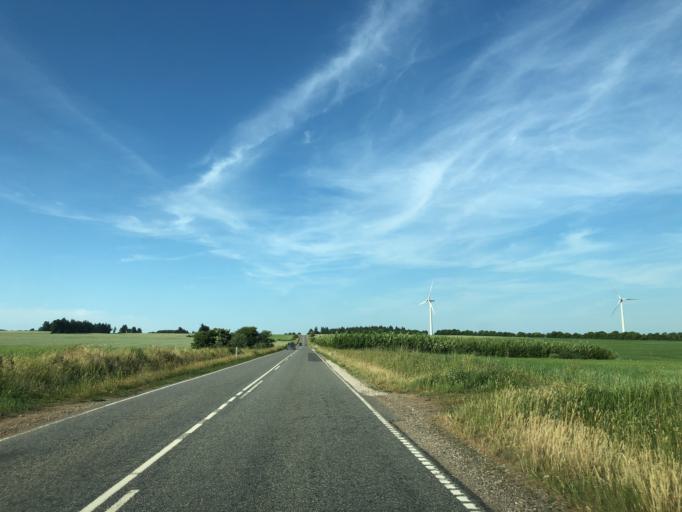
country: DK
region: Central Jutland
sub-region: Struer Kommune
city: Struer
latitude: 56.4202
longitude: 8.4997
